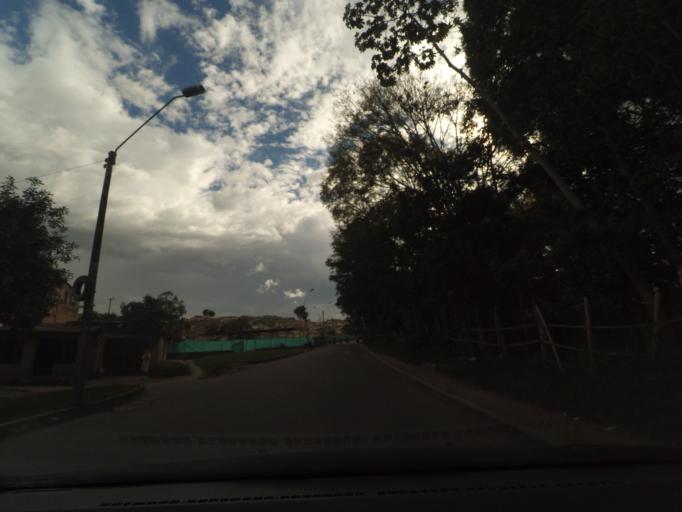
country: CO
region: Cauca
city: Popayan
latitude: 2.4446
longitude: -76.6227
